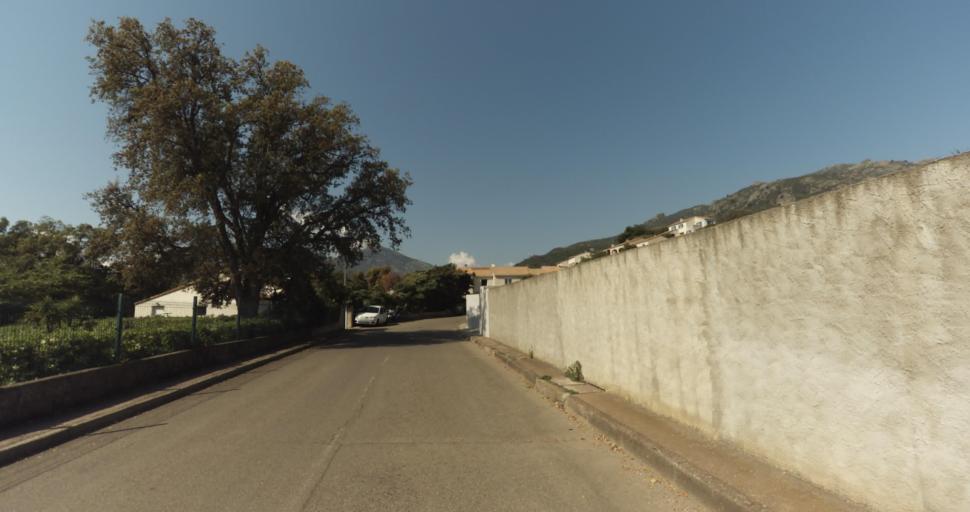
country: FR
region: Corsica
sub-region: Departement de la Haute-Corse
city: Biguglia
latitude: 42.6236
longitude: 9.4330
